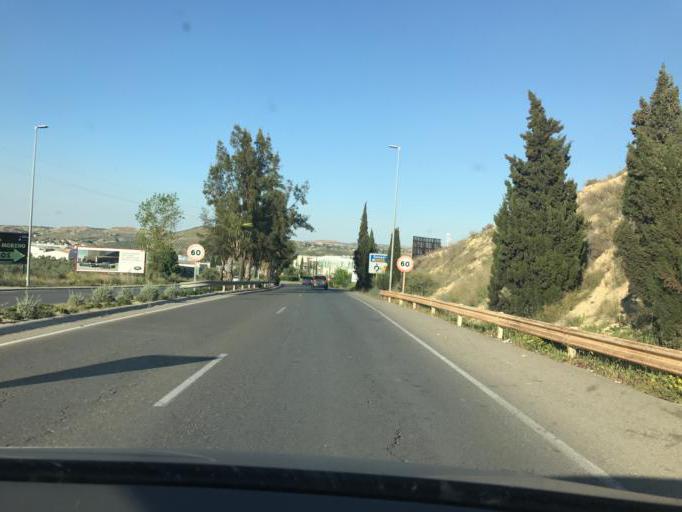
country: ES
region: Andalusia
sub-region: Provincia de Jaen
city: Jaen
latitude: 37.7751
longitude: -3.7609
